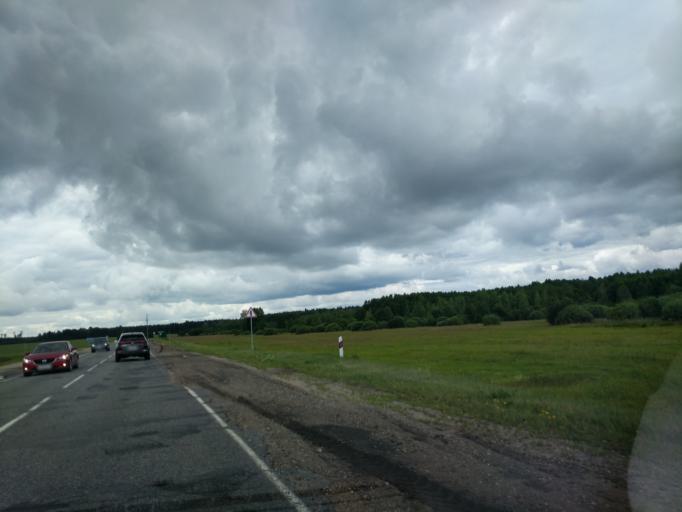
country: BY
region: Minsk
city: Il'ya
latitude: 54.4768
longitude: 27.2589
